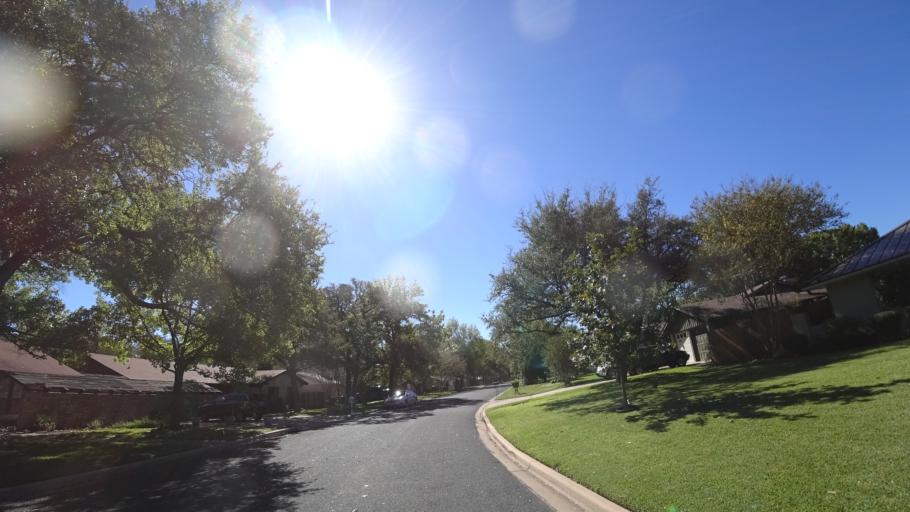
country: US
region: Texas
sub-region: Travis County
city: Rollingwood
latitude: 30.2253
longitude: -97.7957
